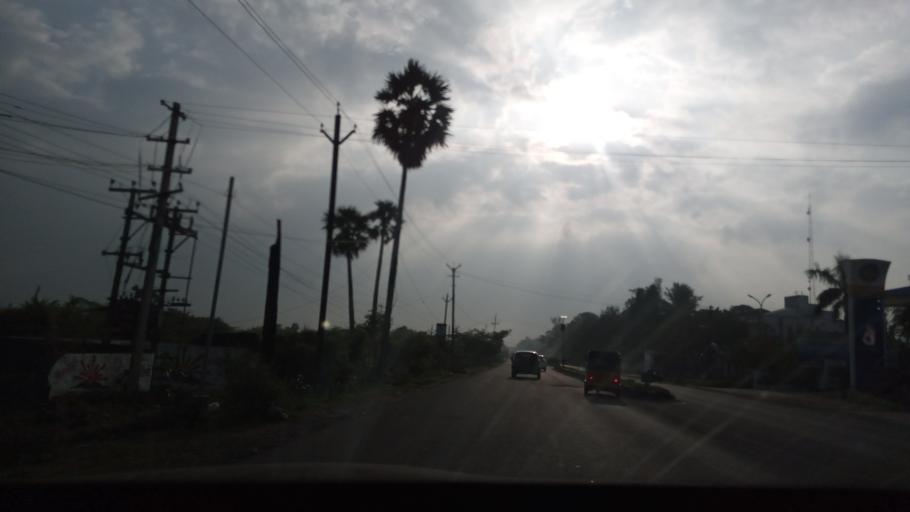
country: IN
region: Tamil Nadu
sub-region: Kancheepuram
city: Vandalur
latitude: 12.8680
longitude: 80.1136
